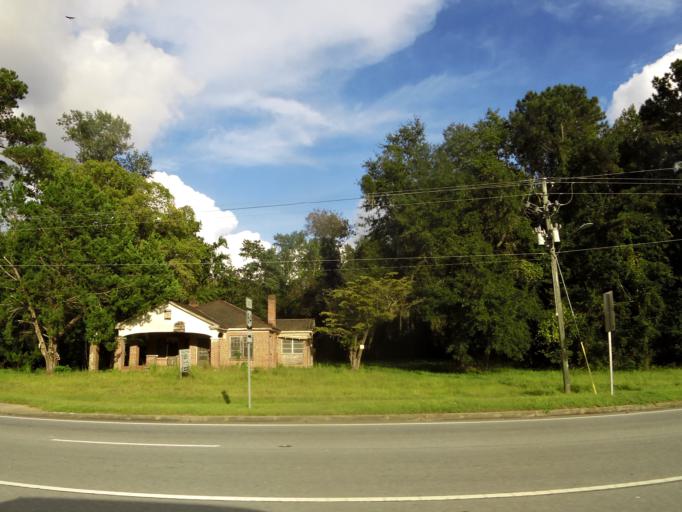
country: US
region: Georgia
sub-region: Liberty County
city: Midway
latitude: 31.7993
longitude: -81.4329
